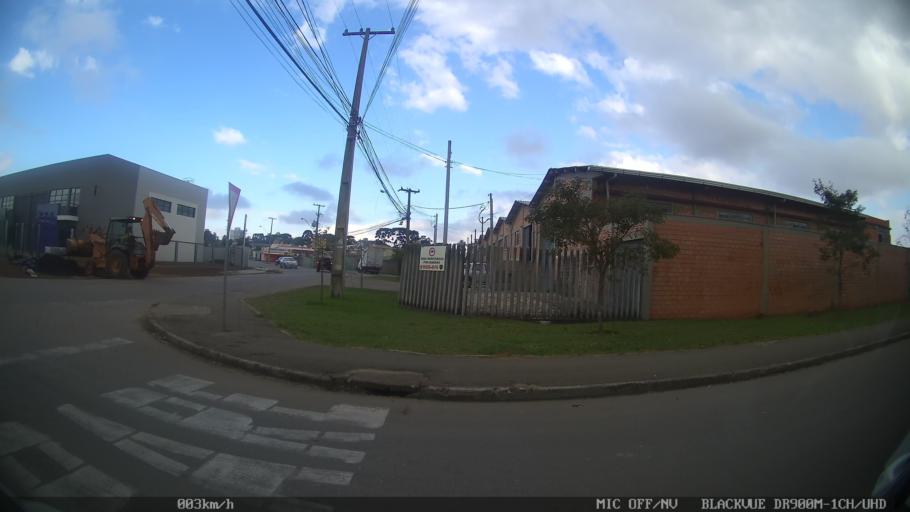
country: BR
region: Parana
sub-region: Pinhais
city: Pinhais
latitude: -25.4364
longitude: -49.1963
